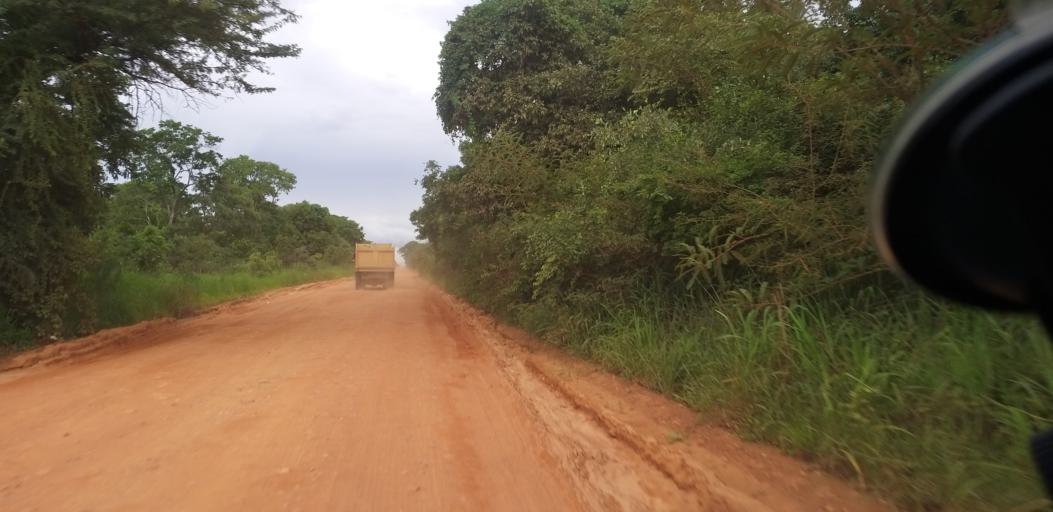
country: ZM
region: Lusaka
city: Lusaka
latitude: -15.1991
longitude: 28.4401
